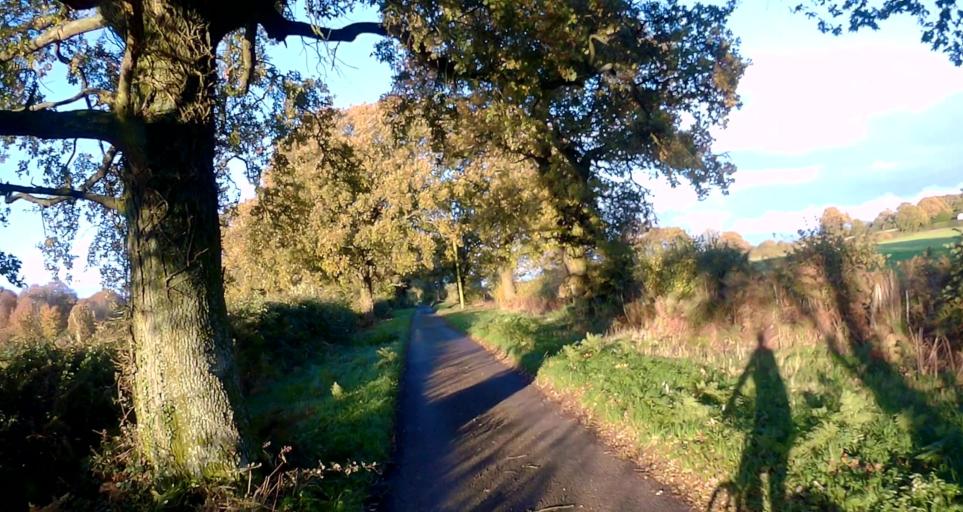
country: GB
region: England
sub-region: Hampshire
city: Basingstoke
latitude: 51.2029
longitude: -1.0814
